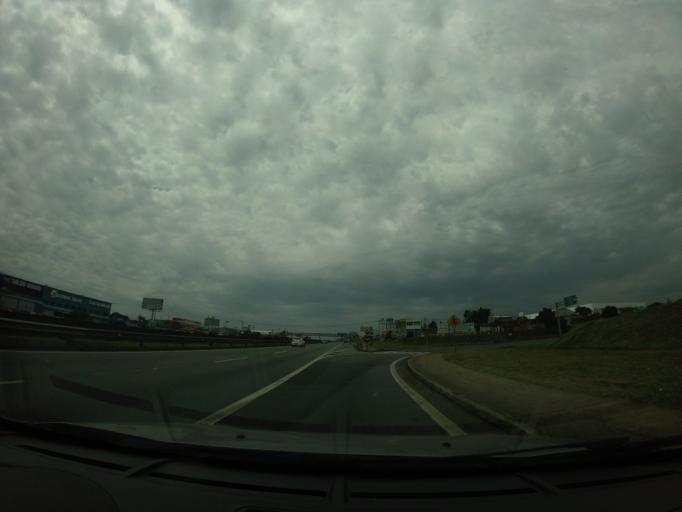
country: BR
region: Sao Paulo
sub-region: Hortolandia
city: Hortolandia
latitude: -22.8431
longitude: -47.1677
